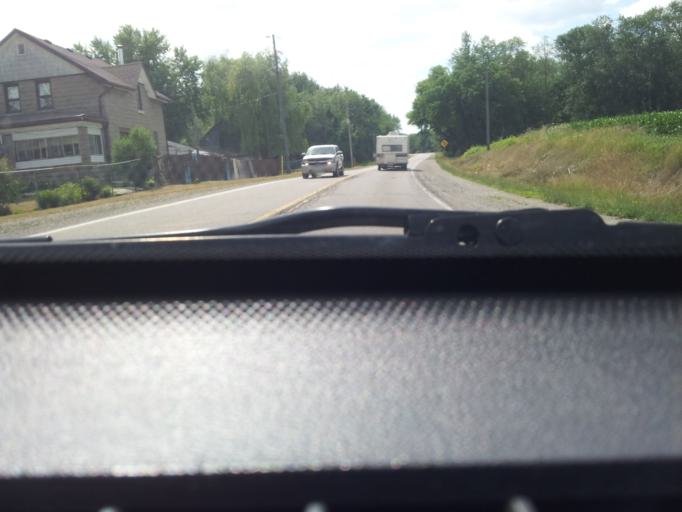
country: CA
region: Ontario
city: Brant
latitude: 43.1008
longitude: -80.4459
